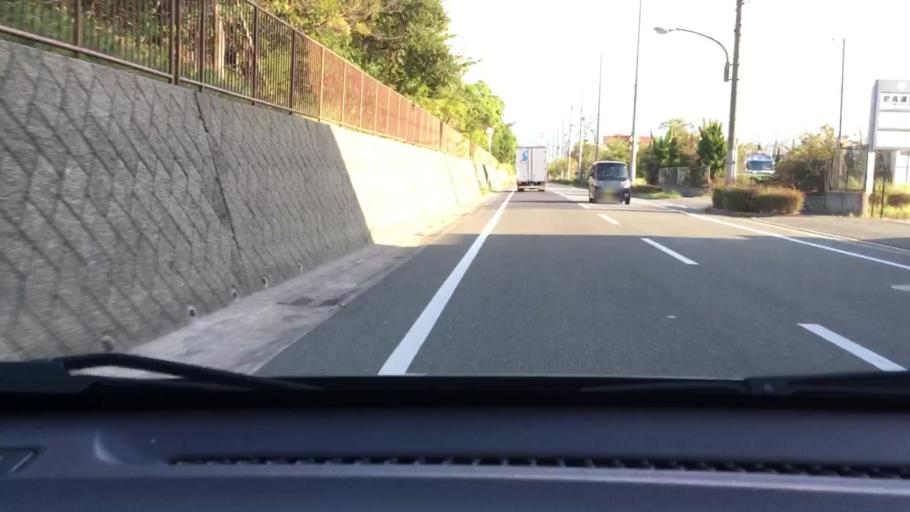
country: JP
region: Hyogo
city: Ashiya
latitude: 34.6853
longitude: 135.2763
